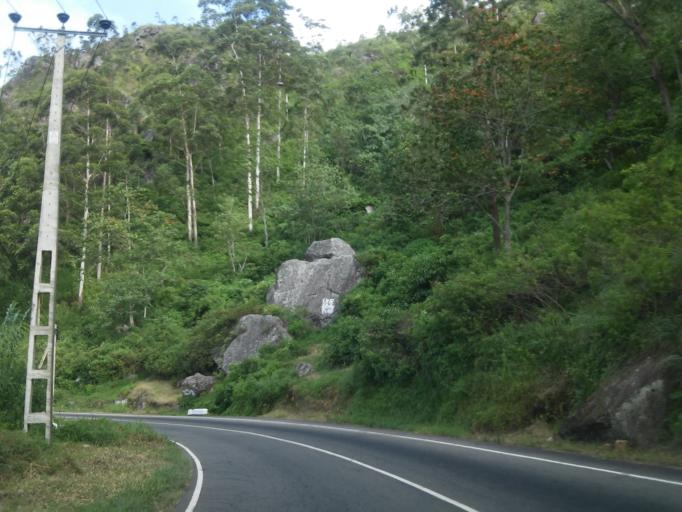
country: LK
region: Uva
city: Haputale
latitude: 6.7622
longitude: 80.9497
